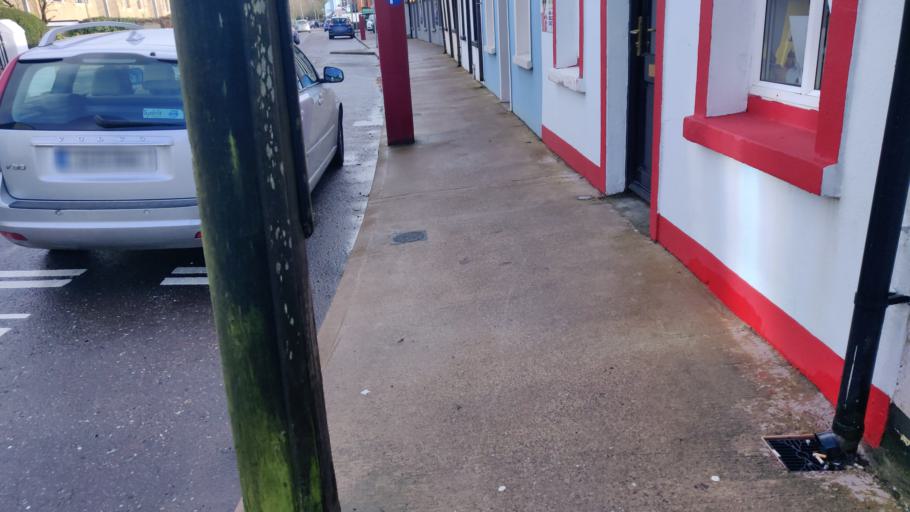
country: IE
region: Munster
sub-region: County Cork
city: Cork
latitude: 51.8767
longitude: -8.4351
